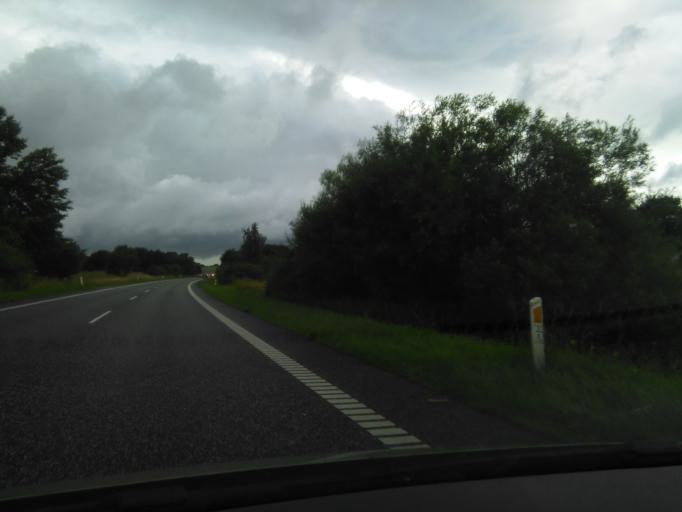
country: DK
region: Central Jutland
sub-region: Skanderborg Kommune
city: Skanderborg
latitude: 56.0485
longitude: 9.8873
